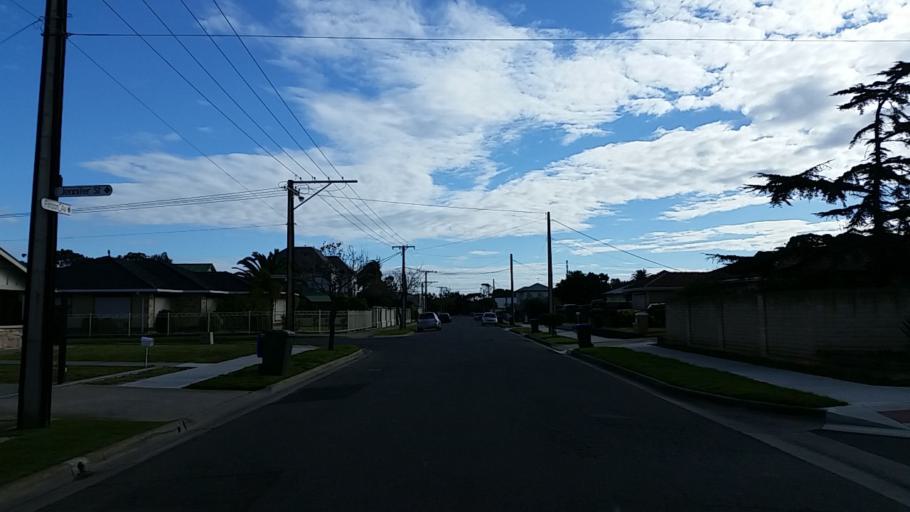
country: AU
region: South Australia
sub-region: Charles Sturt
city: Seaton
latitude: -34.8935
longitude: 138.5170
